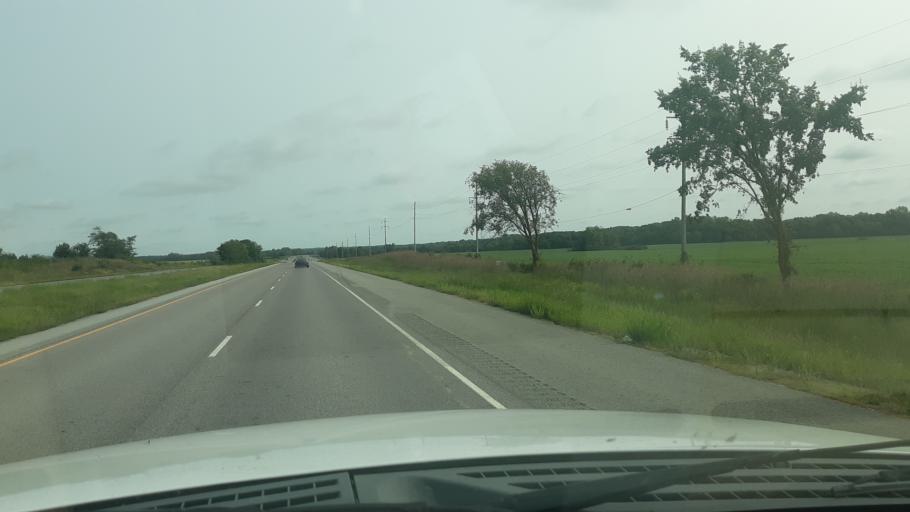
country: US
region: Illinois
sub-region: Saline County
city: Eldorado
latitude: 37.8574
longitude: -88.4055
